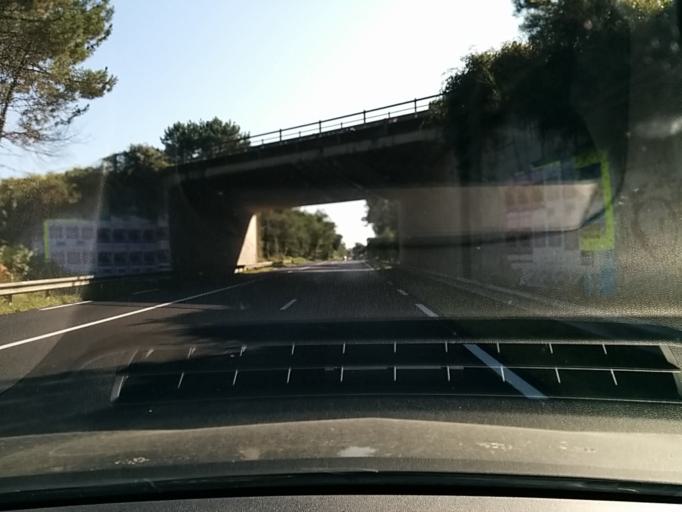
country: FR
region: Aquitaine
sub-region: Departement des Landes
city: Labenne
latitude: 43.6030
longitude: -1.4157
